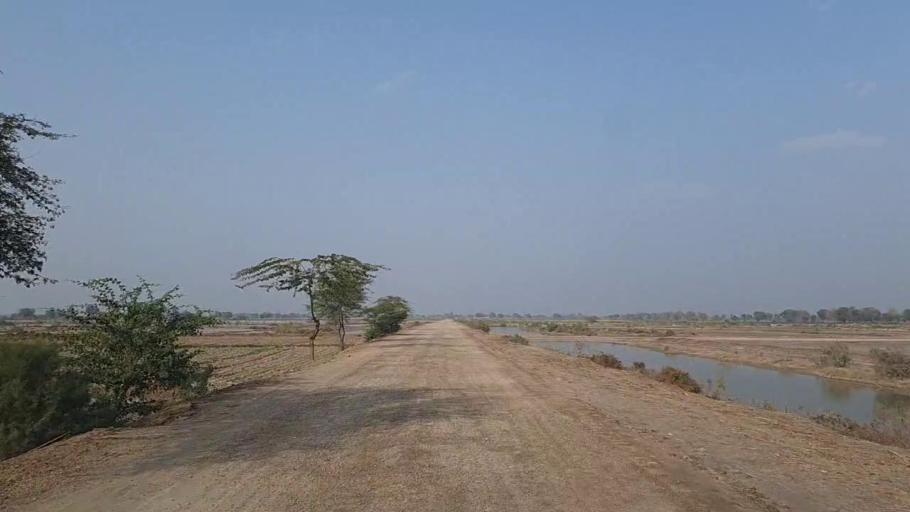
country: PK
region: Sindh
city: Nawabshah
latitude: 26.3400
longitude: 68.4738
